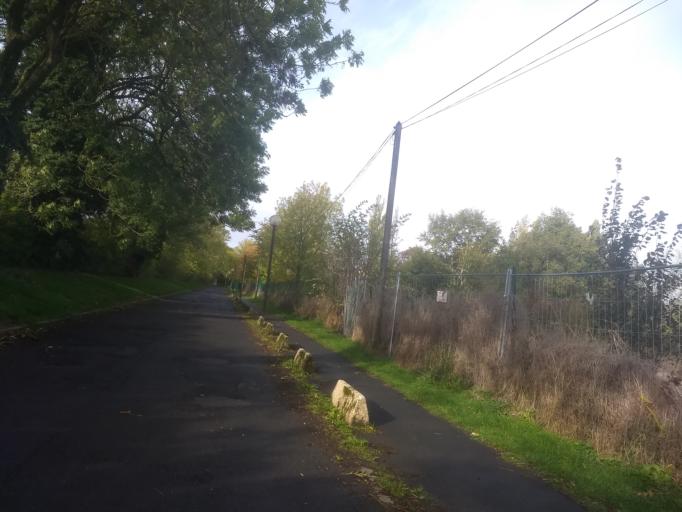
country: FR
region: Nord-Pas-de-Calais
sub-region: Departement du Pas-de-Calais
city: Dainville
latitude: 50.2947
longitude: 2.7397
